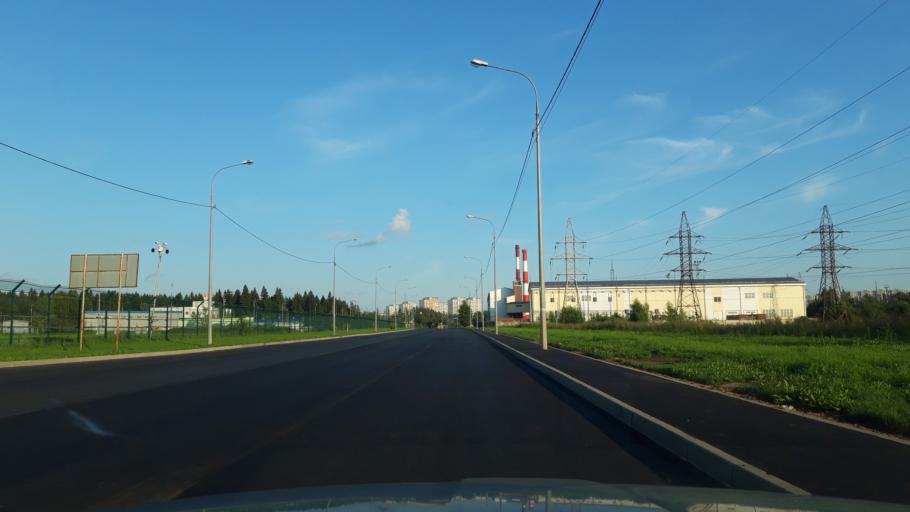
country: RU
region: Moskovskaya
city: Alabushevo
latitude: 56.0004
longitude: 37.1552
